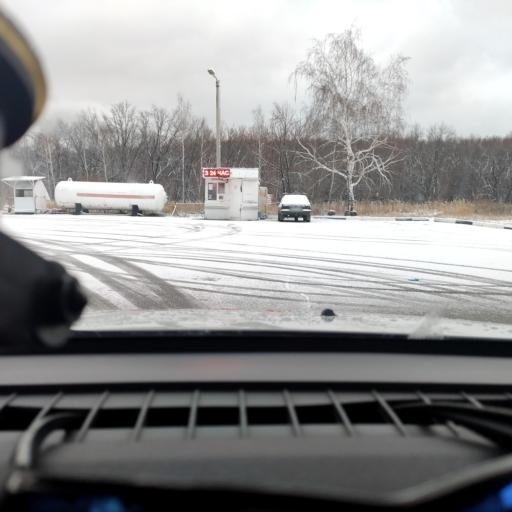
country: RU
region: Samara
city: Novokuybyshevsk
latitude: 52.9829
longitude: 49.8784
